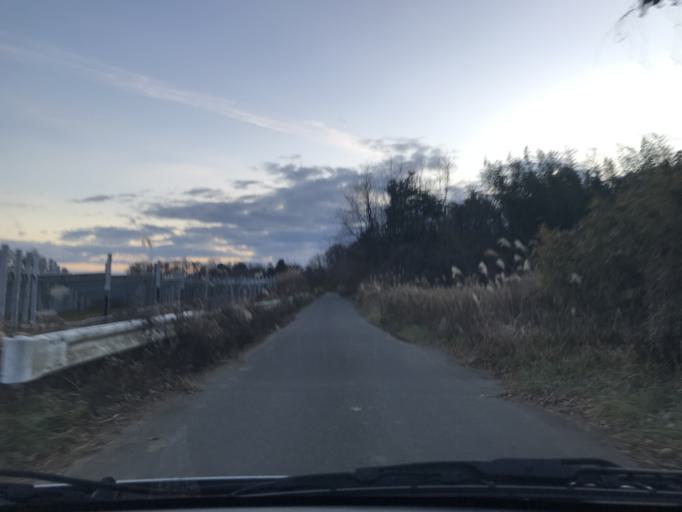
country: JP
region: Iwate
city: Ichinoseki
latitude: 38.8325
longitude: 141.0946
